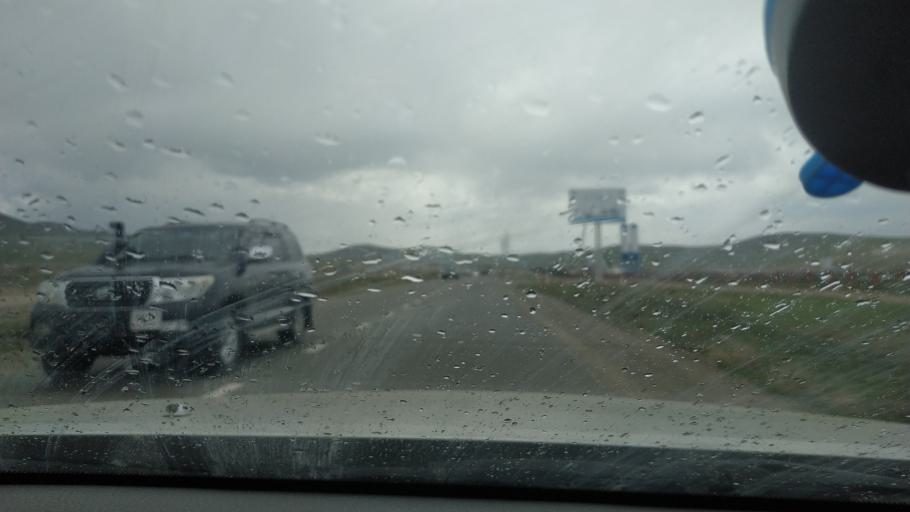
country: MN
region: Ulaanbaatar
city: Ulaanbaatar
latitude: 47.8225
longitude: 106.7633
